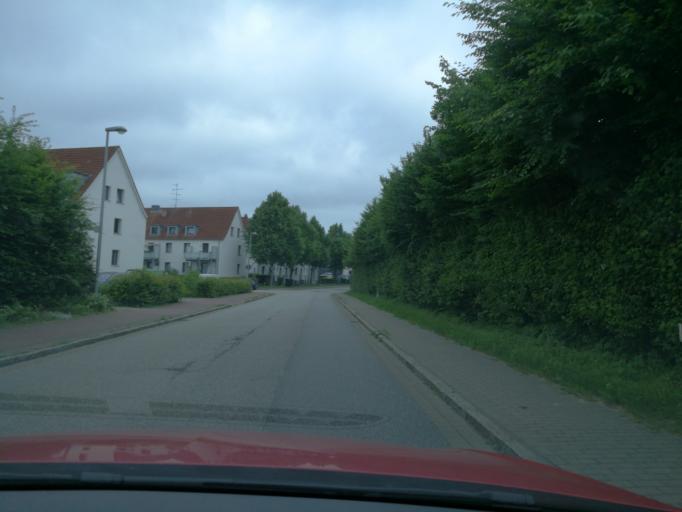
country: DE
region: Schleswig-Holstein
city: Politz
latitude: 53.7975
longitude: 10.3832
